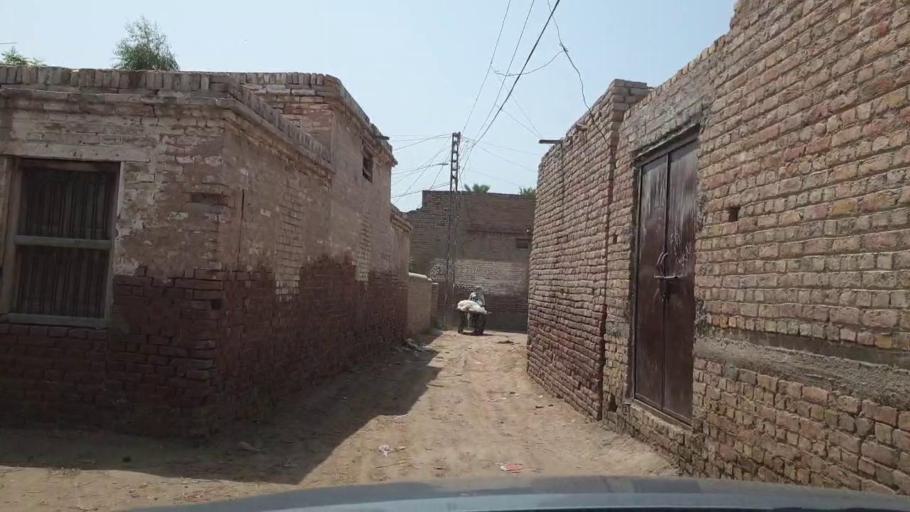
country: PK
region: Sindh
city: Madeji
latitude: 27.7853
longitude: 68.4336
